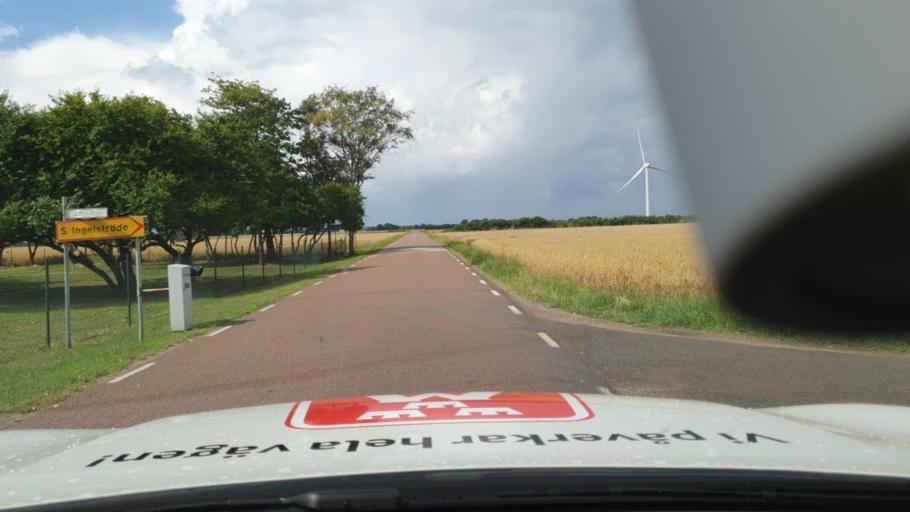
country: SE
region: Skane
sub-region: Hoganas Kommun
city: Hoganas
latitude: 56.1625
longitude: 12.6422
